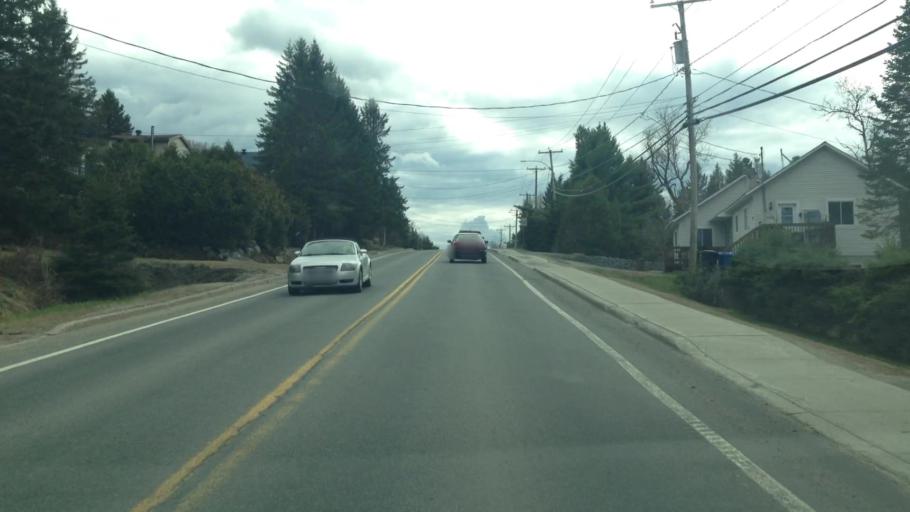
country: CA
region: Quebec
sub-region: Laurentides
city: Sainte-Adele
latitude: 46.0276
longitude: -74.0642
